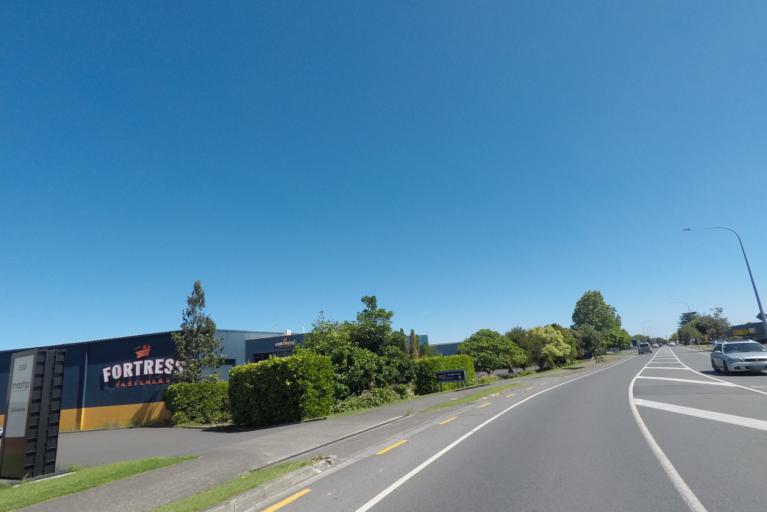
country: NZ
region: Auckland
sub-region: Auckland
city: Rosebank
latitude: -36.8776
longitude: 174.6700
